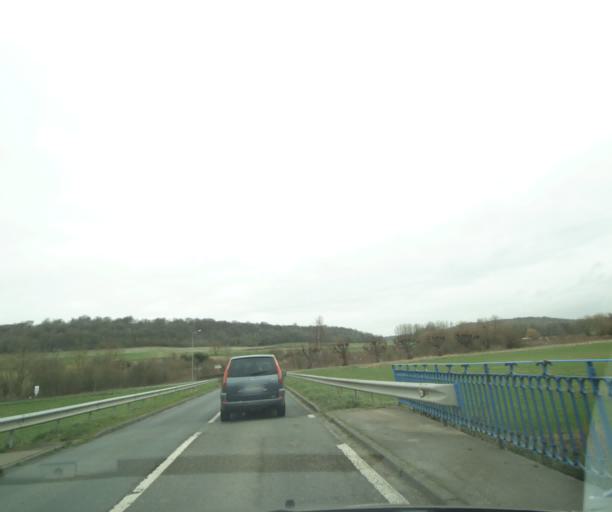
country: FR
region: Picardie
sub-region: Departement de l'Oise
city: Noyon
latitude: 49.5774
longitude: 3.0318
